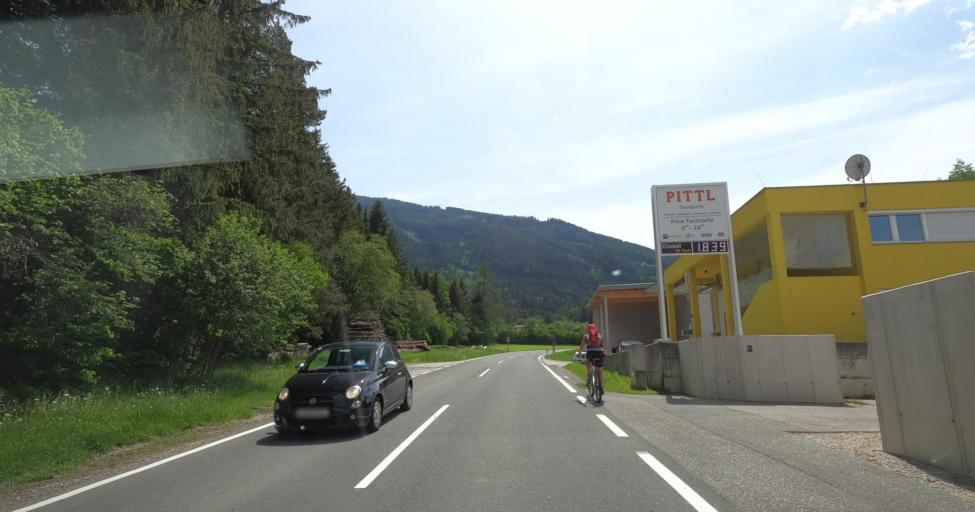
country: AT
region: Tyrol
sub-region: Politischer Bezirk Innsbruck Land
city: Sistrans
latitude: 47.2281
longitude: 11.4299
